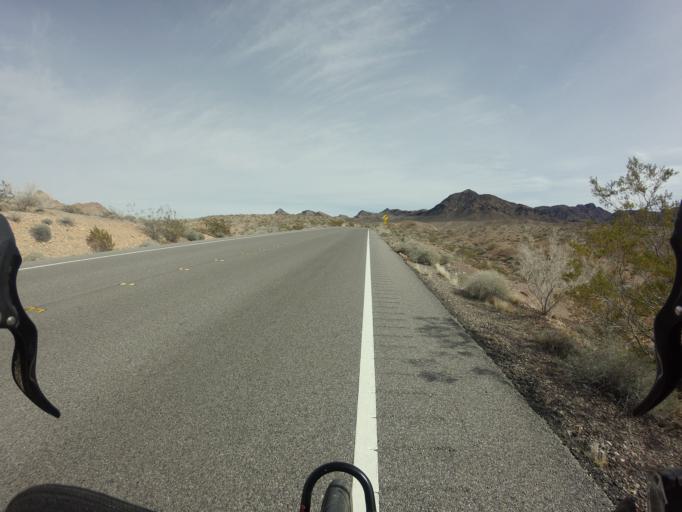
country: US
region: Nevada
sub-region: Clark County
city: Boulder City
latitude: 36.1964
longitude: -114.6863
